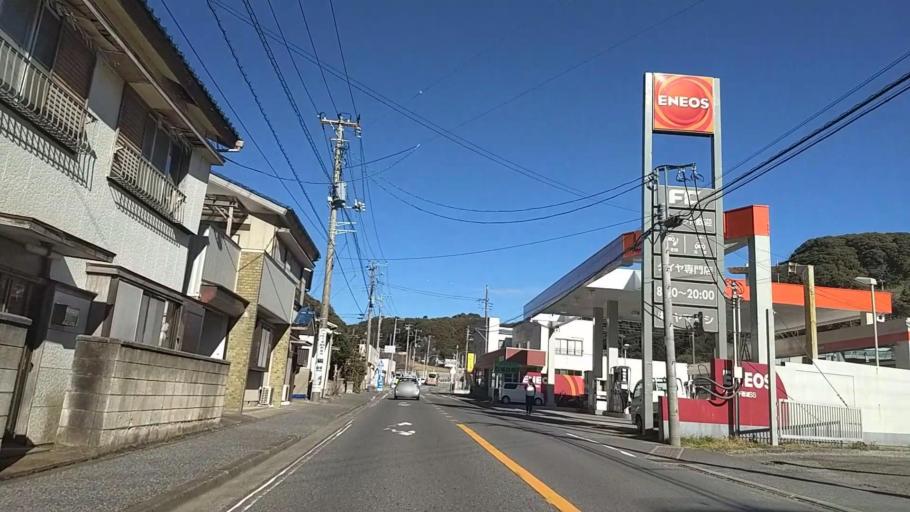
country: JP
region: Chiba
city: Katsuura
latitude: 35.1527
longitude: 140.3189
